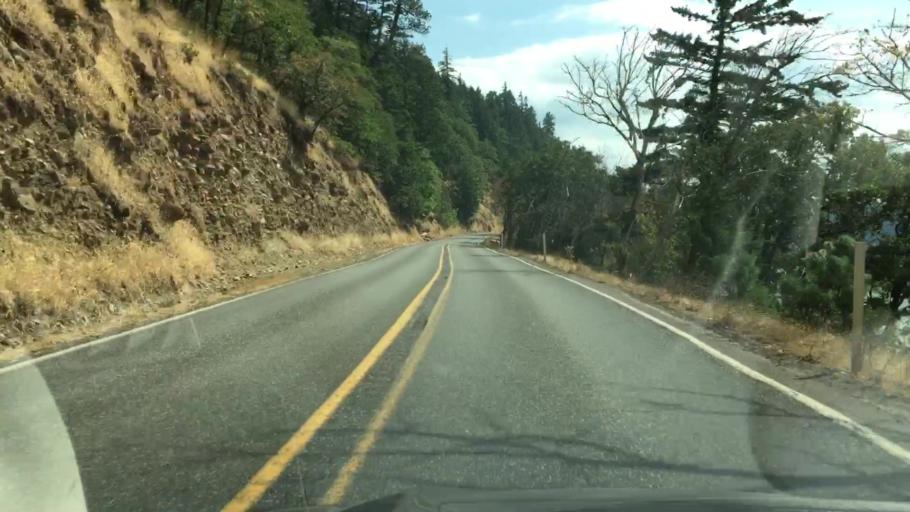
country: US
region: Oregon
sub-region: Hood River County
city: Hood River
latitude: 45.7339
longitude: -121.5211
